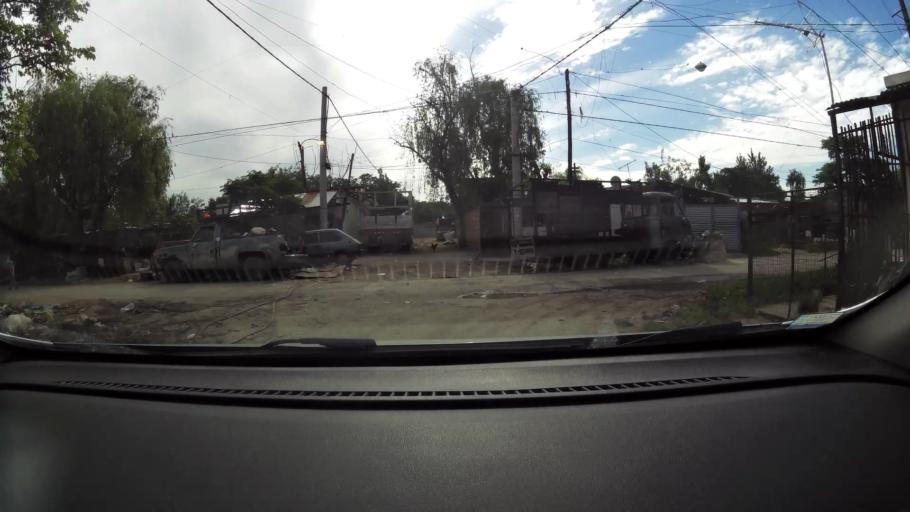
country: AR
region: Santa Fe
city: Granadero Baigorria
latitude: -32.9109
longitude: -60.7047
